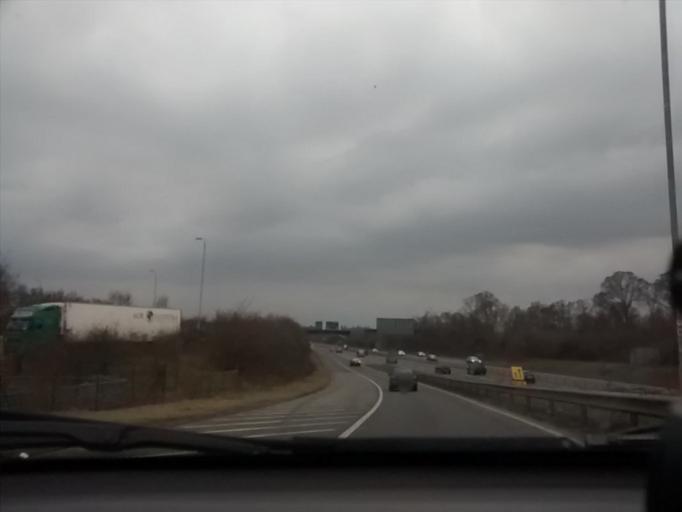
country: GB
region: England
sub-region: Cambridgeshire
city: Sawston
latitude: 52.1285
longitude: 0.2226
